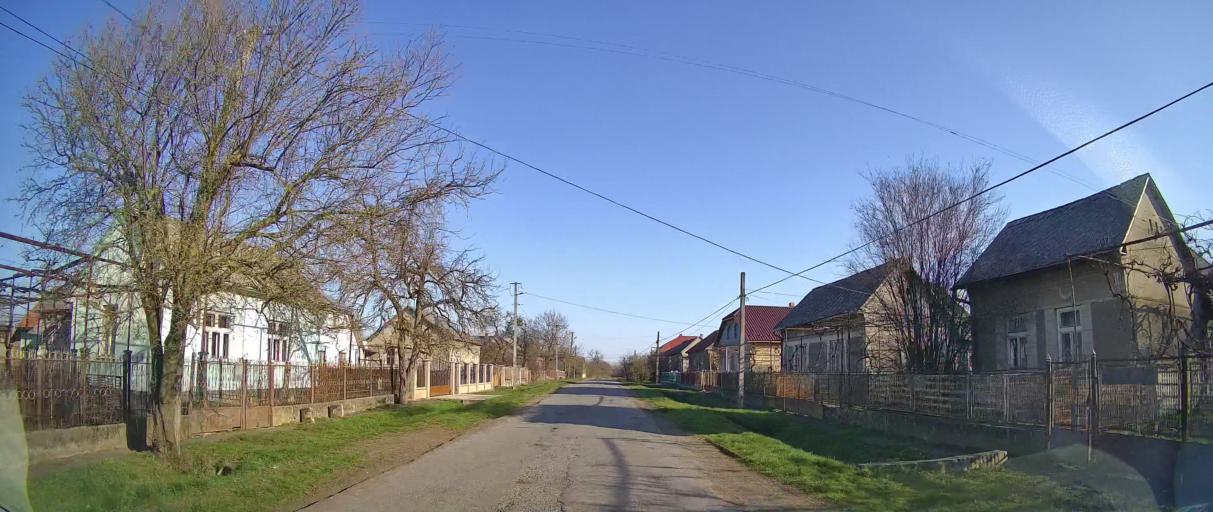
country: UA
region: Zakarpattia
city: Storozhnytsya
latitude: 48.5673
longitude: 22.1737
